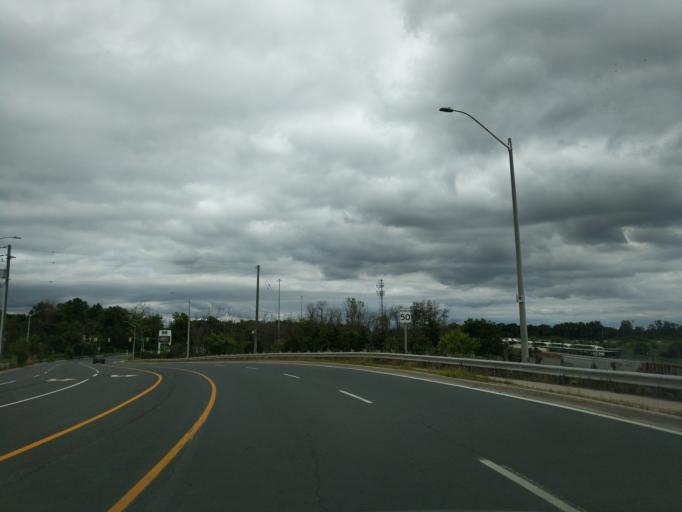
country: CA
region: Ontario
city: Hamilton
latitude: 43.3117
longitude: -79.8583
